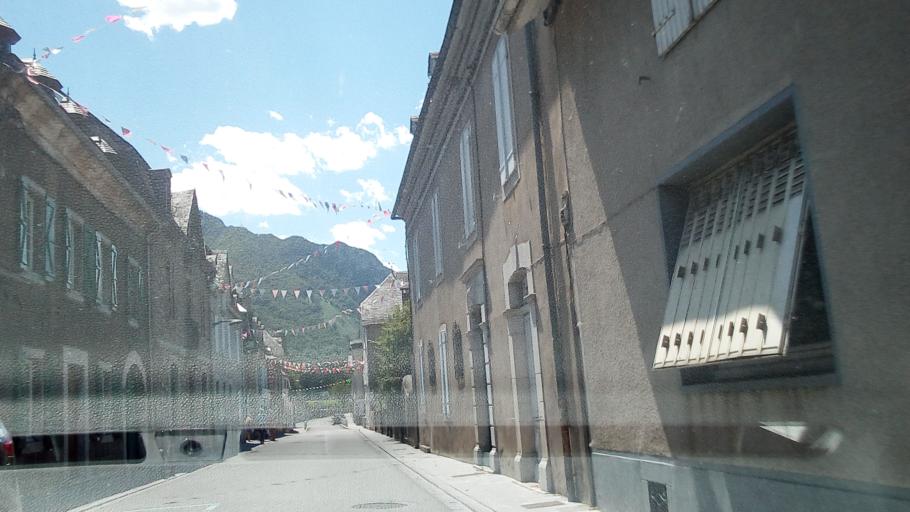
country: FR
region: Aquitaine
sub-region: Departement des Pyrenees-Atlantiques
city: Arette
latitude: 42.9996
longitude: -0.6010
